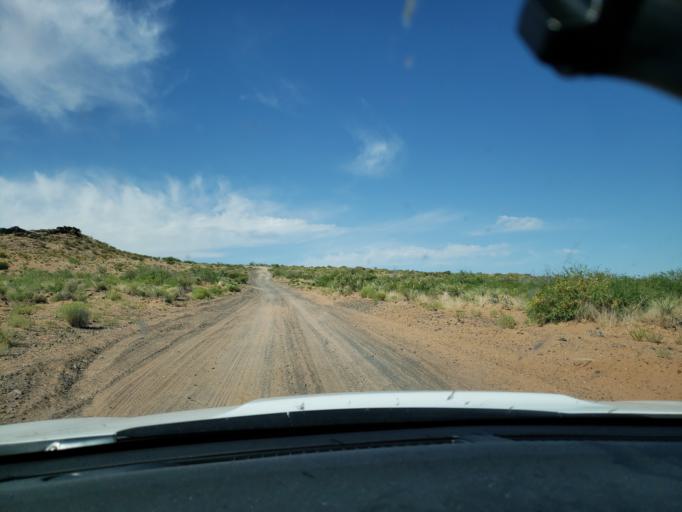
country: US
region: New Mexico
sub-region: Dona Ana County
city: San Miguel
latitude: 32.0802
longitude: -106.7929
